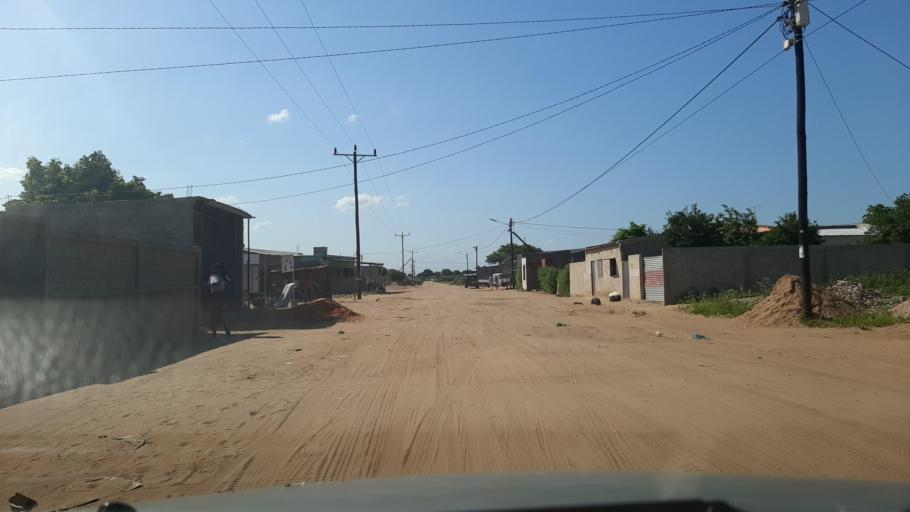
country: MZ
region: Maputo
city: Matola
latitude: -25.7988
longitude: 32.4906
